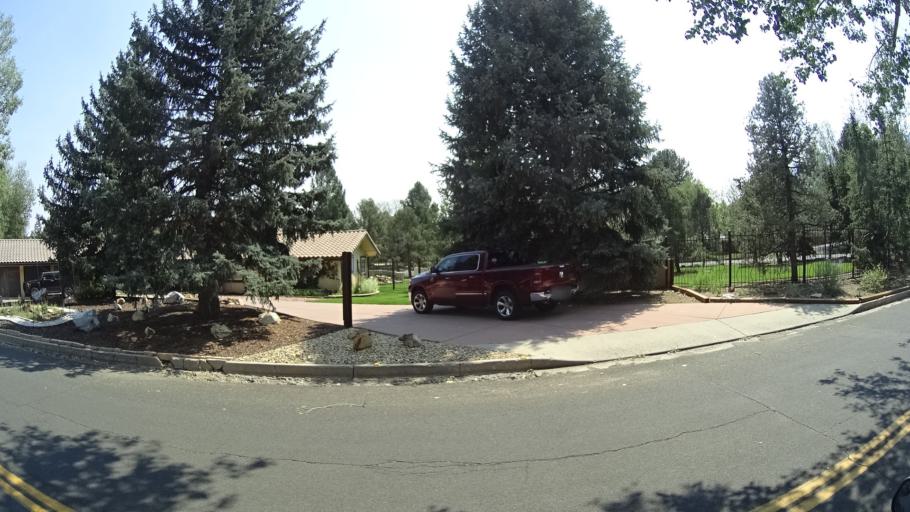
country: US
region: Colorado
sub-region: El Paso County
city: Colorado Springs
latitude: 38.7974
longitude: -104.8406
